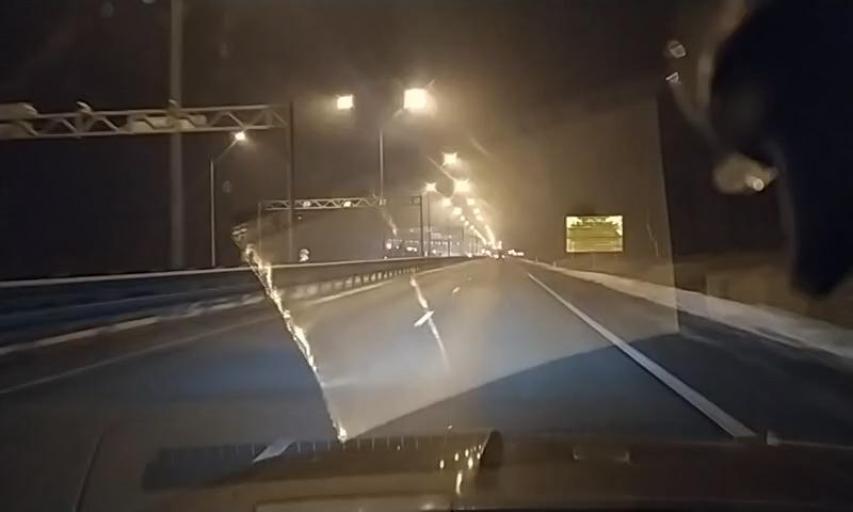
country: RU
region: Leningrad
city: Bugry
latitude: 60.1025
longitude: 30.3851
